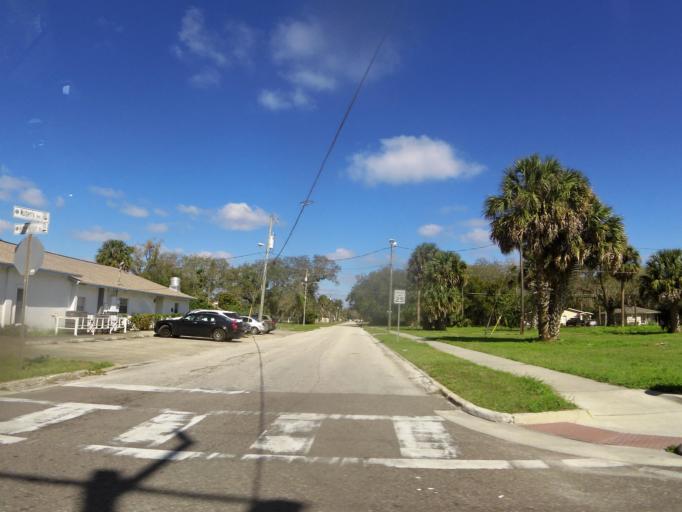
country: US
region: Florida
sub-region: Seminole County
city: Sanford
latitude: 28.8008
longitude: -81.2856
